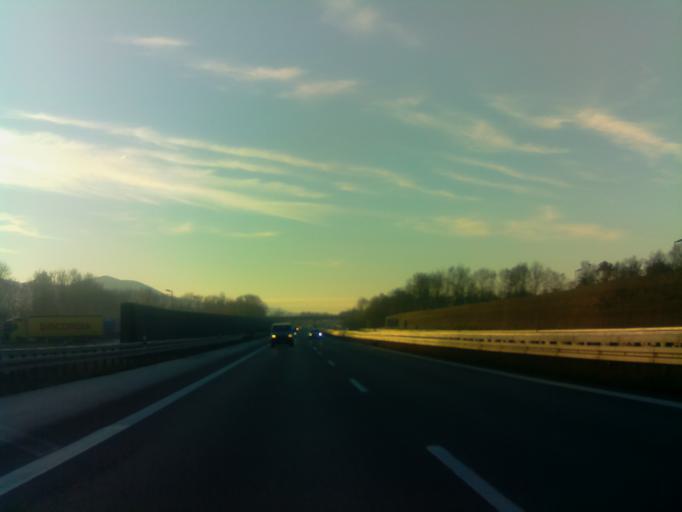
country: DE
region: Baden-Wuerttemberg
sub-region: Karlsruhe Region
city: Weinheim
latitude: 49.5331
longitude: 8.6327
